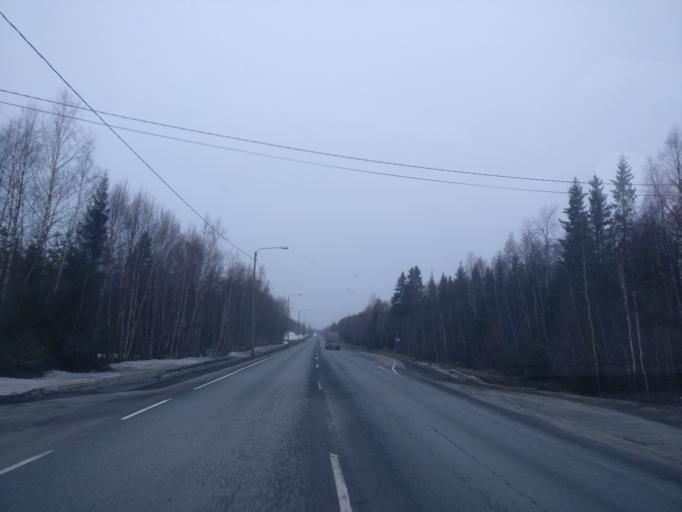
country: FI
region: Lapland
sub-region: Kemi-Tornio
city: Simo
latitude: 65.6748
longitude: 24.8530
